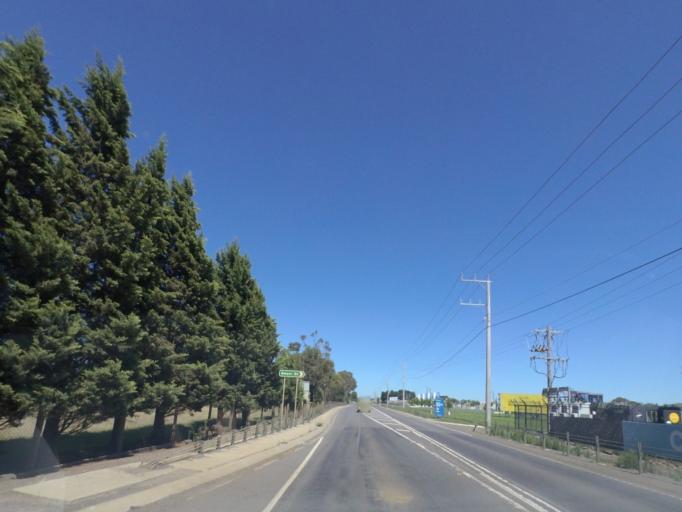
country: AU
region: Victoria
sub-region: Hume
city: Craigieburn
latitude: -37.5413
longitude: 144.9566
